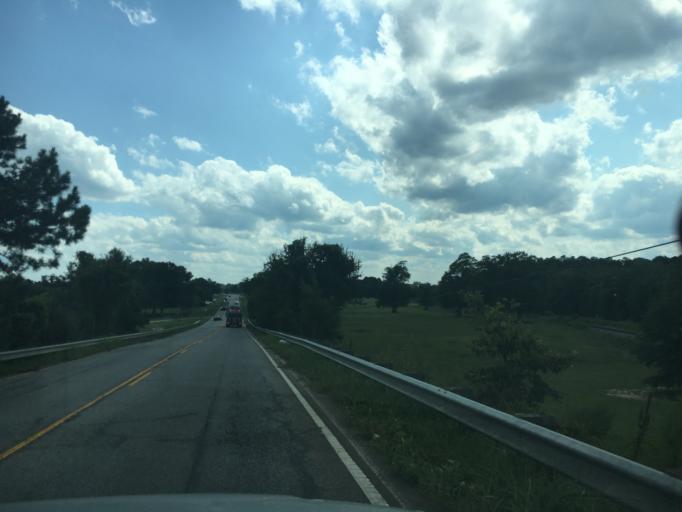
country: US
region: South Carolina
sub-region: Anderson County
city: Williamston
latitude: 34.5977
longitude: -82.4986
